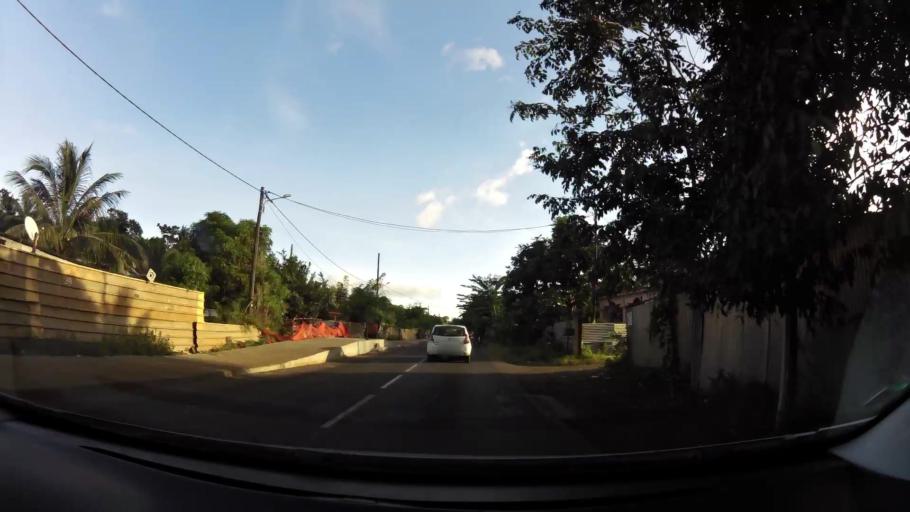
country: YT
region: Dembeni
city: Dembeni
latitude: -12.8140
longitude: 45.2013
